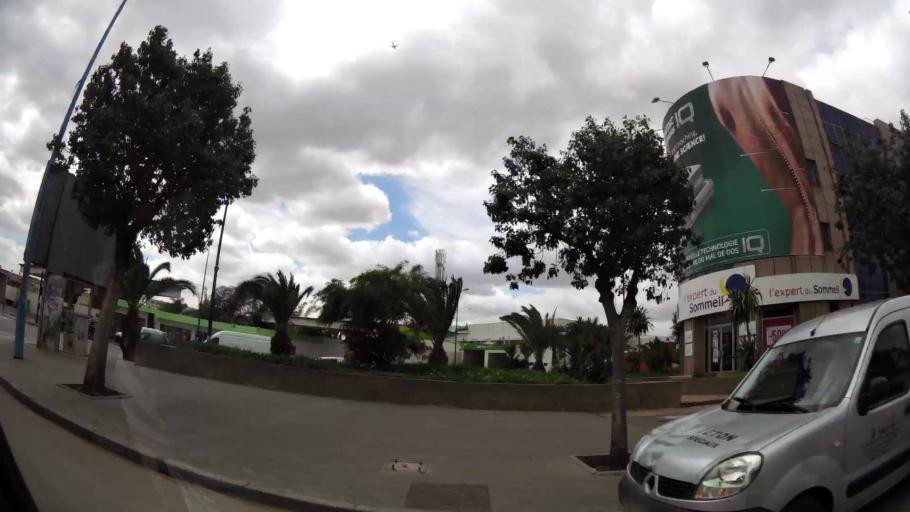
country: MA
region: Grand Casablanca
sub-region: Casablanca
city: Casablanca
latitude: 33.6043
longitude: -7.5460
